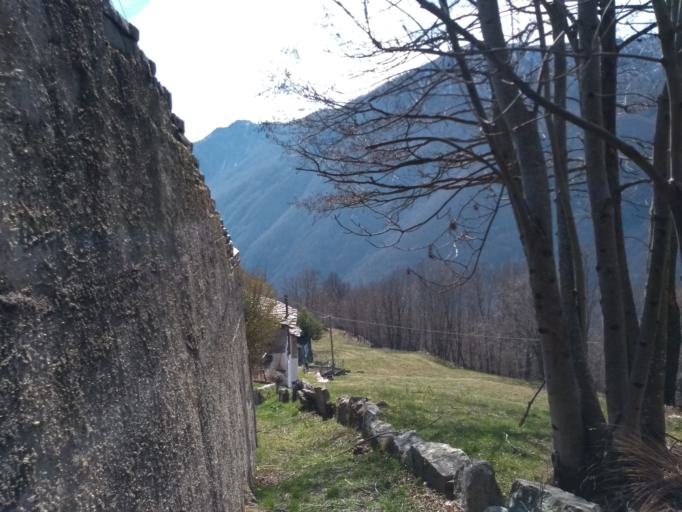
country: IT
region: Piedmont
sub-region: Provincia di Torino
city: Chialamberto
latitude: 45.3682
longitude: 7.3476
